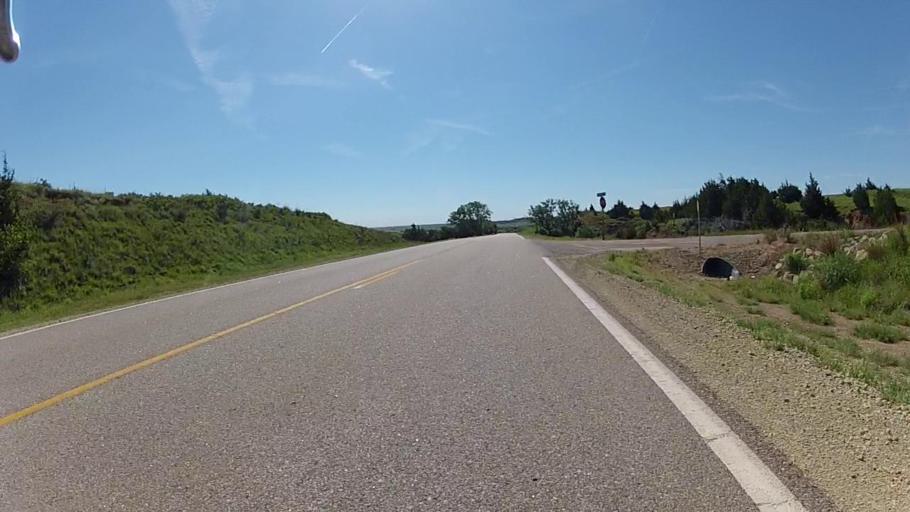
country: US
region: Kansas
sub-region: Barber County
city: Medicine Lodge
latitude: 37.2780
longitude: -98.7388
